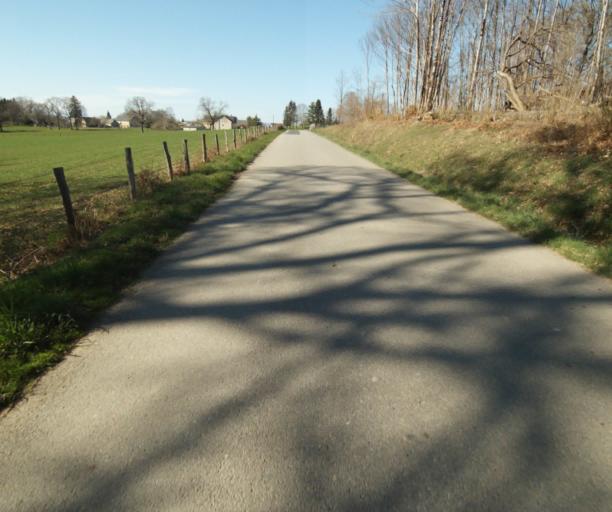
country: FR
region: Limousin
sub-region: Departement de la Correze
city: Chamboulive
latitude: 45.4830
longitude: 1.7136
